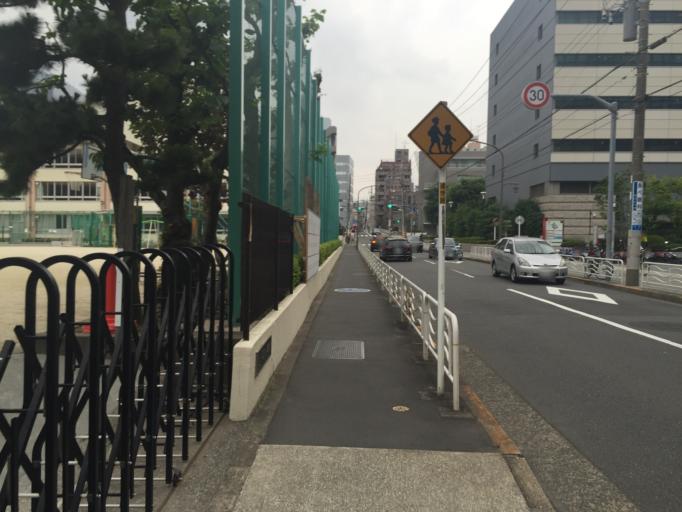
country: JP
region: Tokyo
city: Urayasu
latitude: 35.6674
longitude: 139.8029
